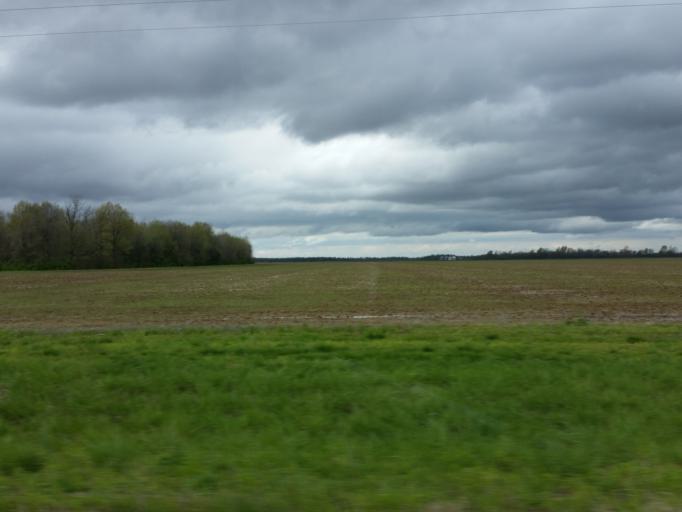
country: US
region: Arkansas
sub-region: Clay County
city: Corning
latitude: 36.5743
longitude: -90.5208
